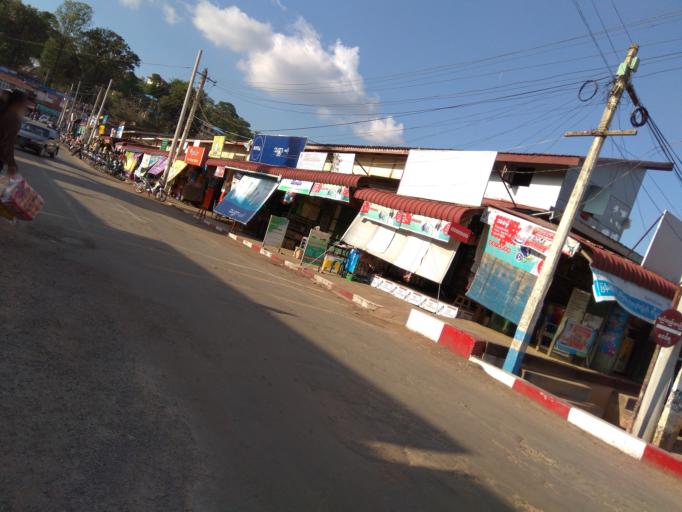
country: MM
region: Mandalay
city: Yamethin
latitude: 20.6350
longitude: 96.5665
